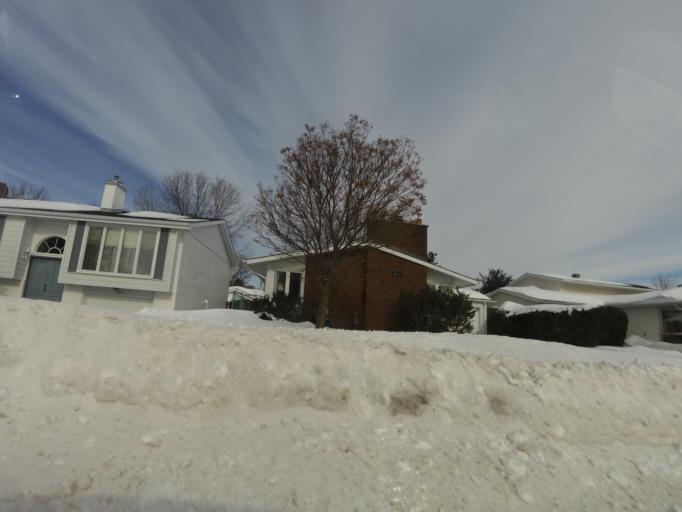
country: CA
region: Ontario
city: Ottawa
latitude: 45.4426
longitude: -75.6008
